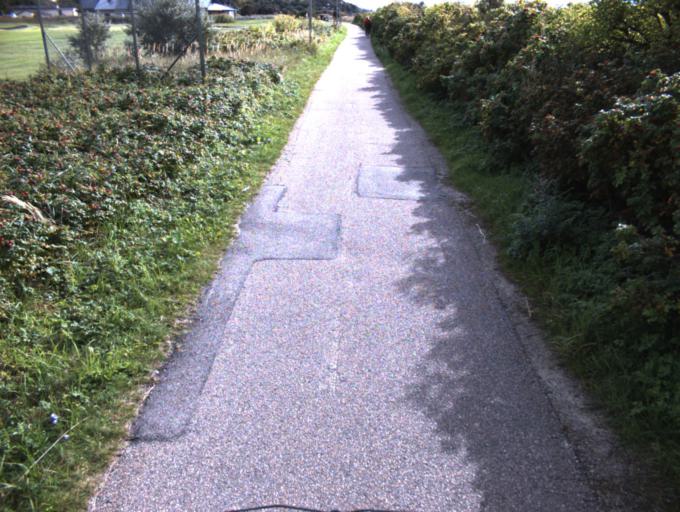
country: SE
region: Skane
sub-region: Helsingborg
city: Rydeback
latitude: 55.9775
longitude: 12.7553
